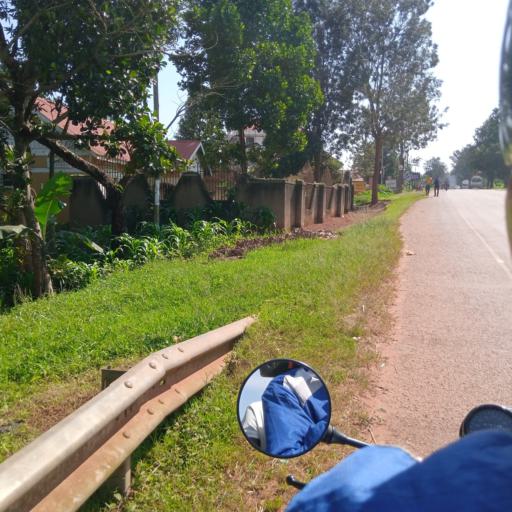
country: UG
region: Central Region
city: Masaka
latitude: -0.3493
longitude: 31.7255
